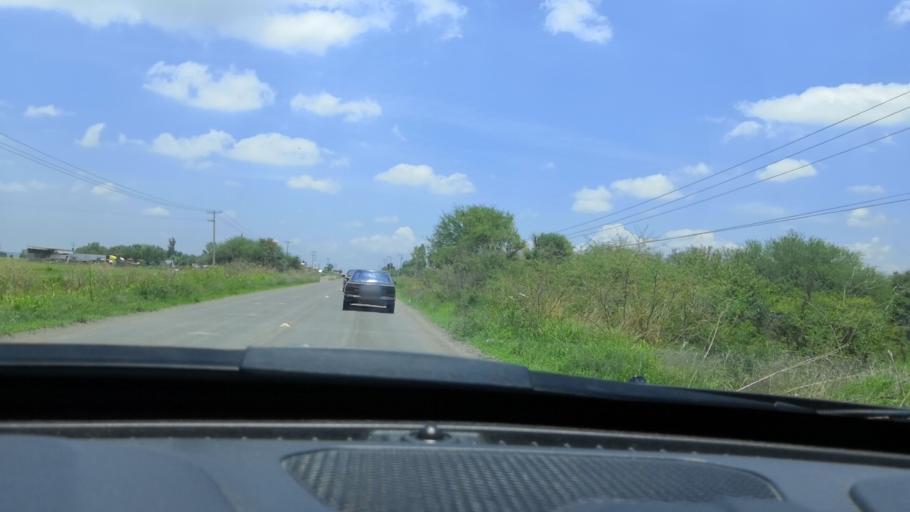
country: MX
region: Guanajuato
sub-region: Silao de la Victoria
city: El Refugio de los Sauces
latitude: 21.0091
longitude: -101.5804
